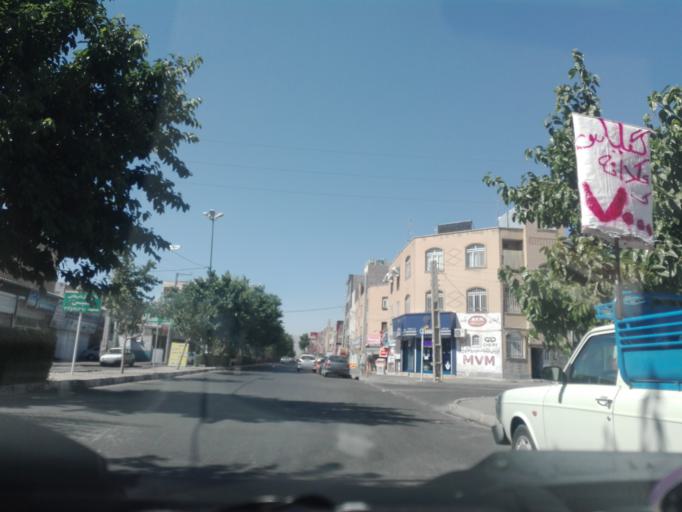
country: IR
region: Tehran
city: Malard
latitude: 35.7190
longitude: 50.9793
